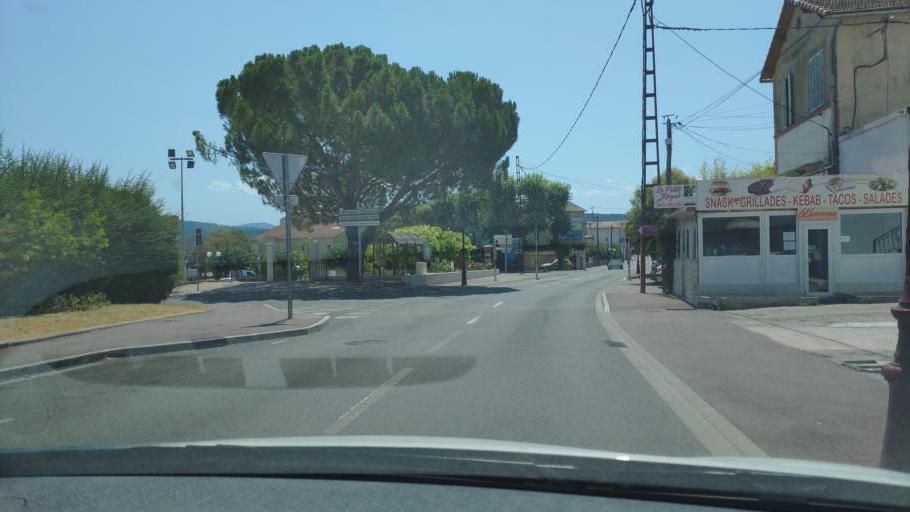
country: FR
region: Provence-Alpes-Cote d'Azur
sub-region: Departement du Var
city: Les Arcs
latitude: 43.4575
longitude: 6.4807
